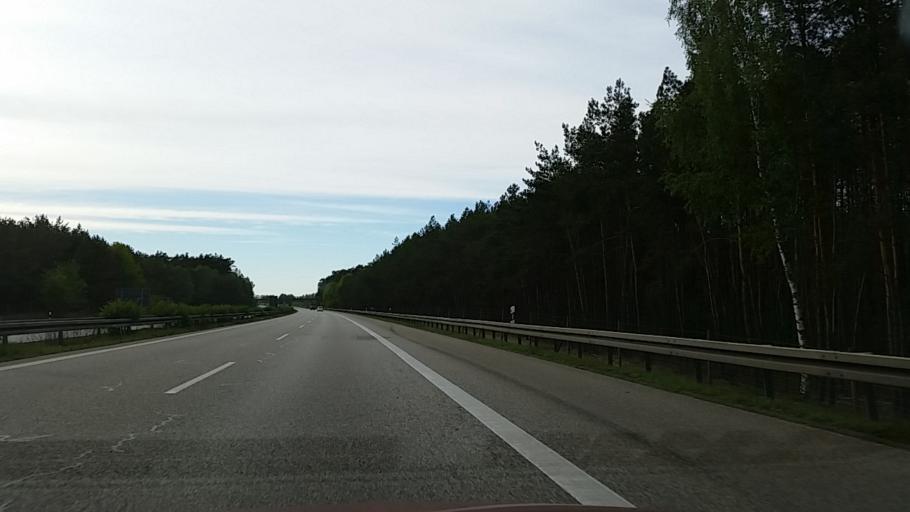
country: DE
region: Mecklenburg-Vorpommern
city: Neustadt-Glewe
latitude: 53.3885
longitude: 11.6081
